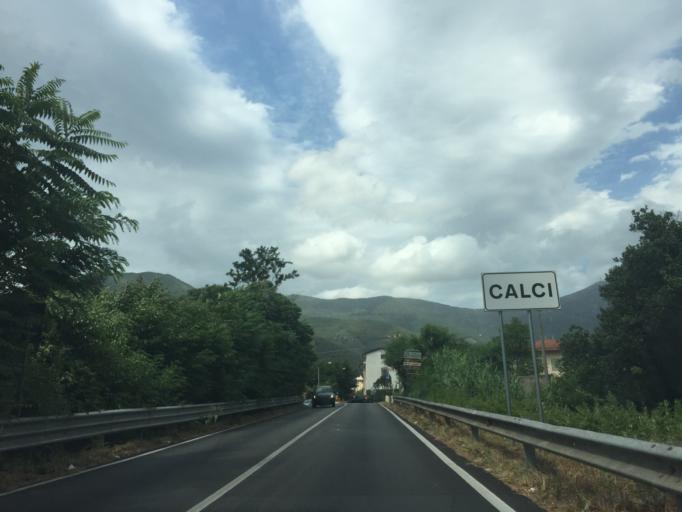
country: IT
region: Tuscany
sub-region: Province of Pisa
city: Calci
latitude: 43.7170
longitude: 10.5102
